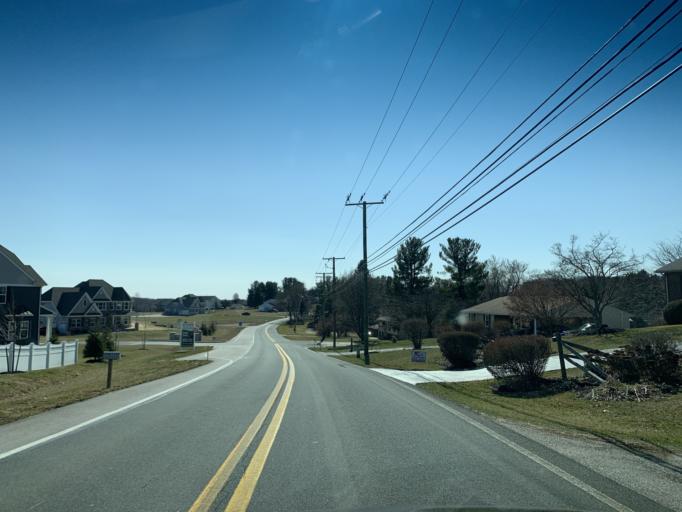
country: US
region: Maryland
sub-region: Carroll County
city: Hampstead
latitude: 39.5900
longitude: -76.8631
